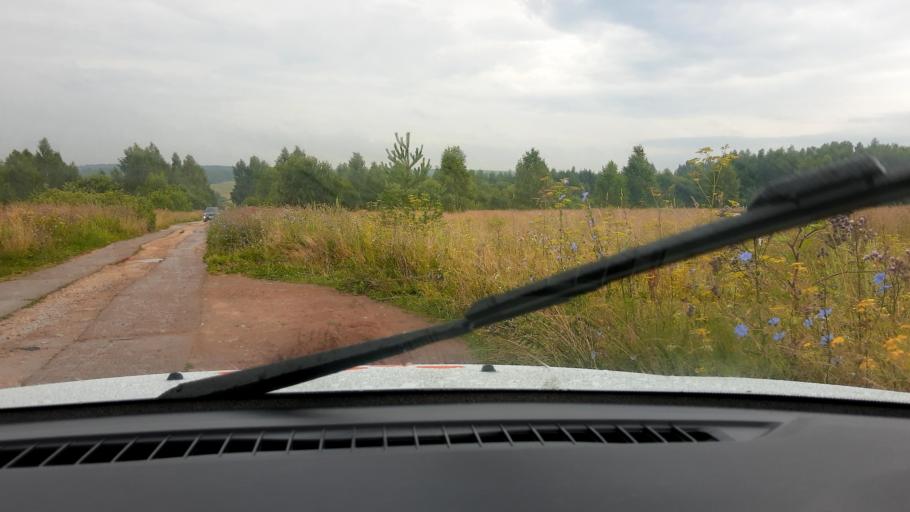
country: RU
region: Nizjnij Novgorod
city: Surovatikha
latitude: 55.9443
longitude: 43.9158
